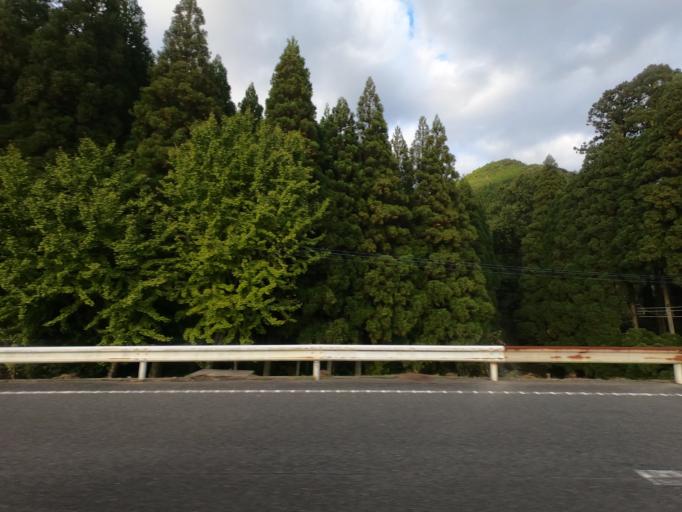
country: JP
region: Kumamoto
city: Minamata
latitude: 32.2457
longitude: 130.4769
